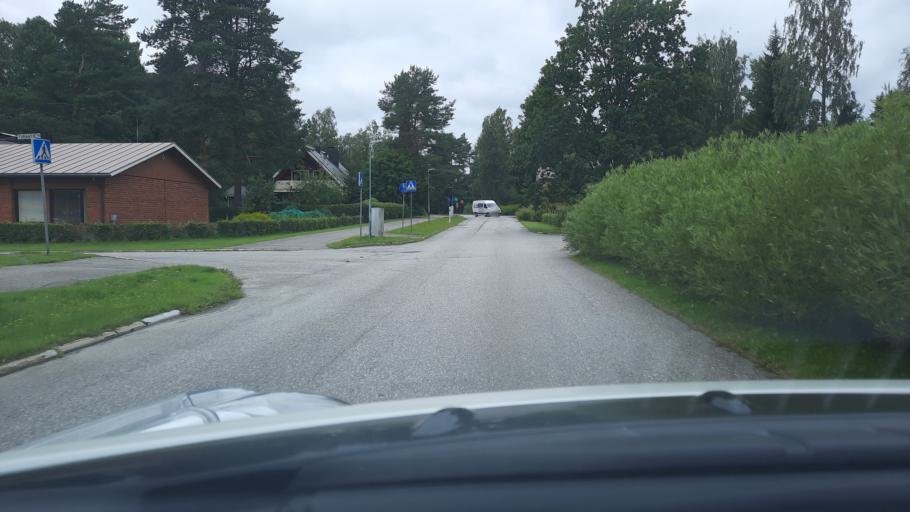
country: FI
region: North Karelia
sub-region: Joensuu
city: Joensuu
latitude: 62.6124
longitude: 29.8338
